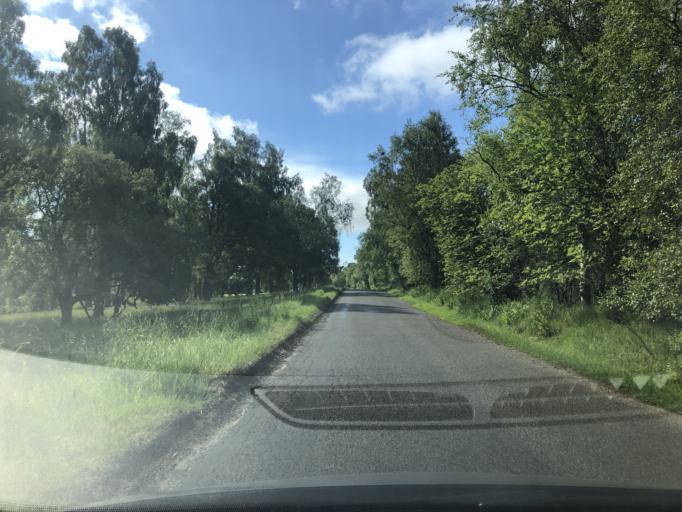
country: GB
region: Scotland
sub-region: Angus
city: Kirriemuir
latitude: 56.7465
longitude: -3.0130
